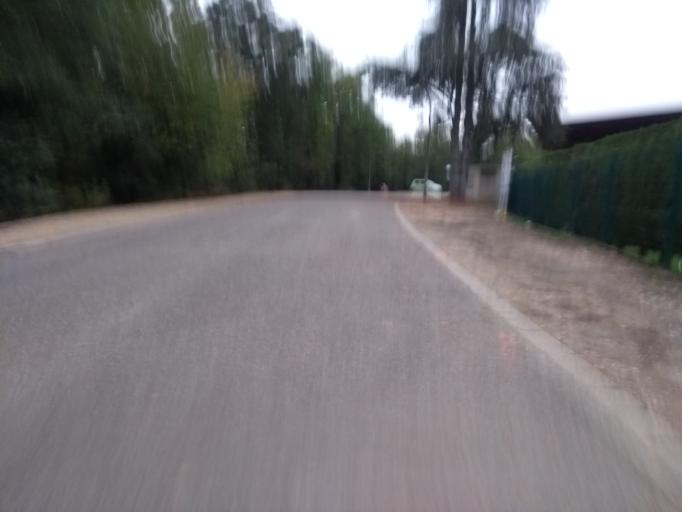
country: FR
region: Aquitaine
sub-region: Departement de la Gironde
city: Talence
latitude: 44.7909
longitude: -0.5970
